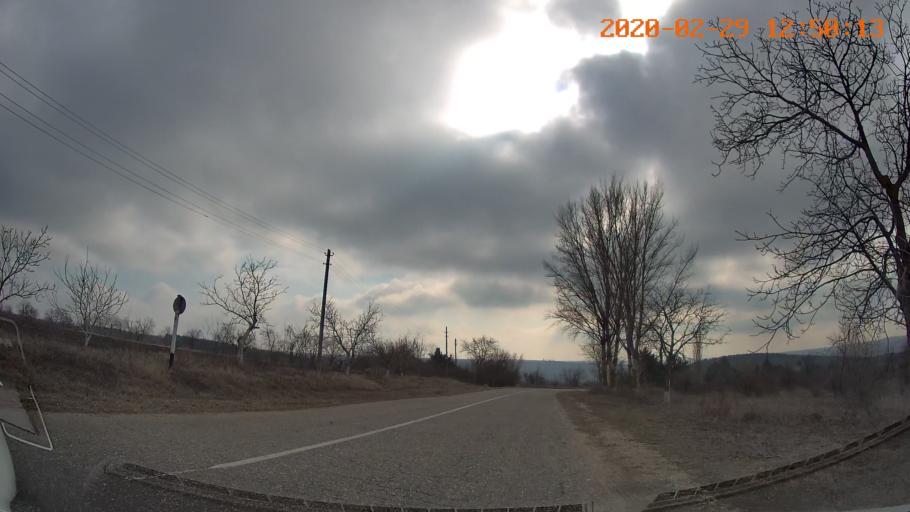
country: MD
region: Telenesti
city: Camenca
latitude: 48.1260
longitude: 28.7410
